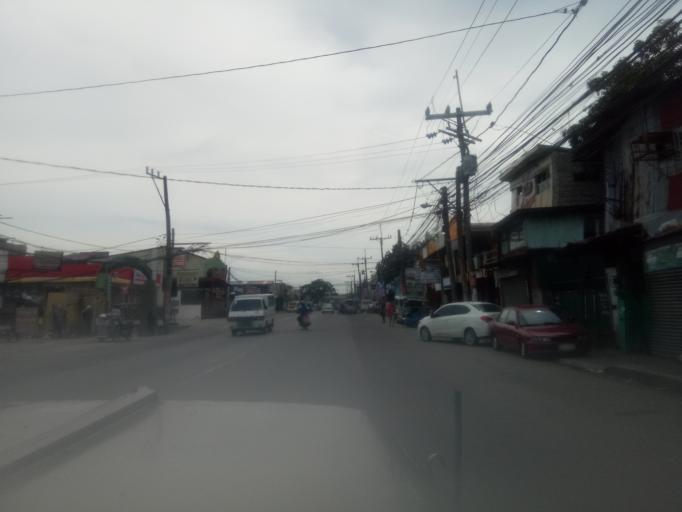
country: PH
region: Calabarzon
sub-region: Province of Cavite
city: Bulihan
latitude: 14.2865
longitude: 121.0010
